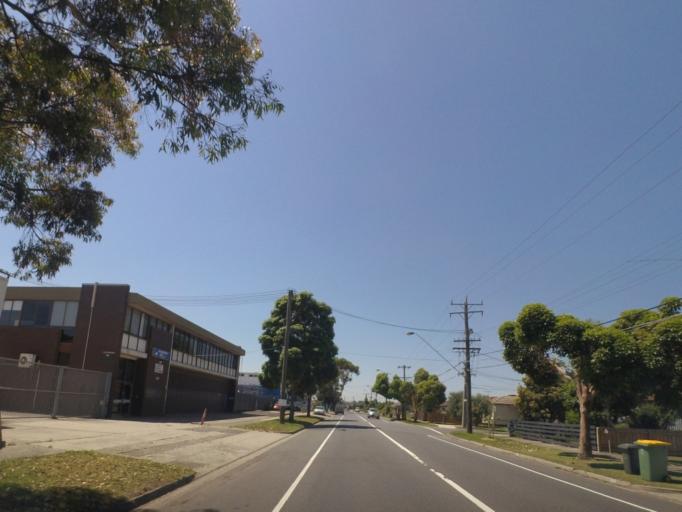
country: AU
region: Victoria
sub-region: Darebin
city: Reservoir
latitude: -37.7098
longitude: 144.9898
